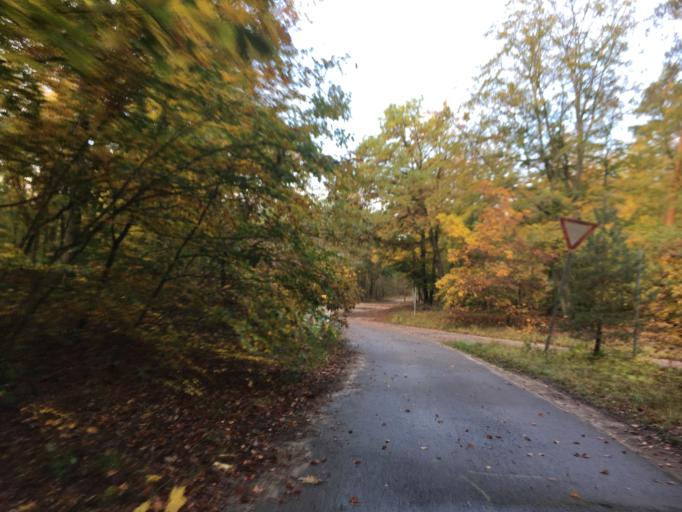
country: DE
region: Brandenburg
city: Wandlitz
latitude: 52.7297
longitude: 13.4606
